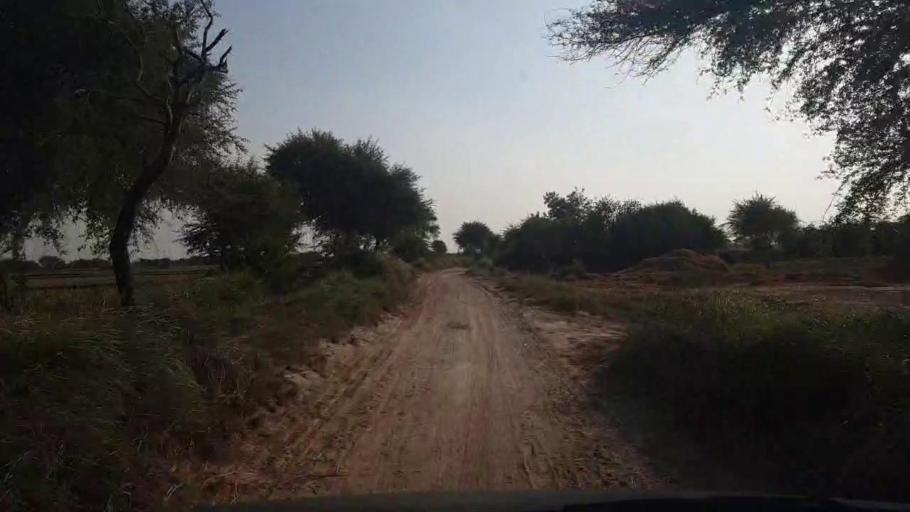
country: PK
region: Sindh
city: Badin
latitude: 24.6320
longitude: 68.7970
